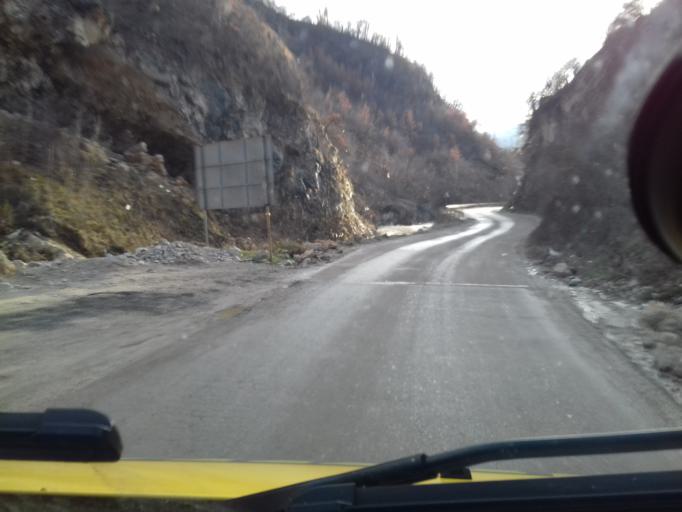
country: BA
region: Federation of Bosnia and Herzegovina
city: Zenica
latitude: 44.2124
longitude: 17.9337
